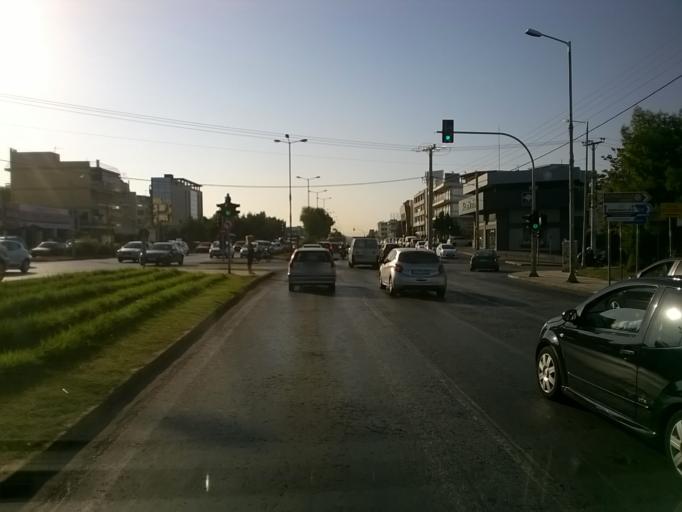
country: GR
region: Attica
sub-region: Nomarchia Athinas
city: Elliniko
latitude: 37.8868
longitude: 23.7505
